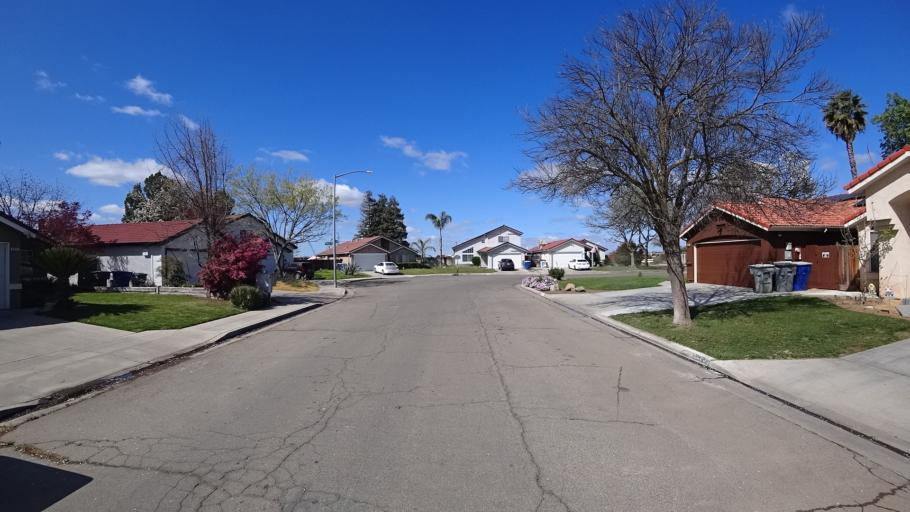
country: US
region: California
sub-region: Fresno County
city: Biola
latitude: 36.8273
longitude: -119.8956
